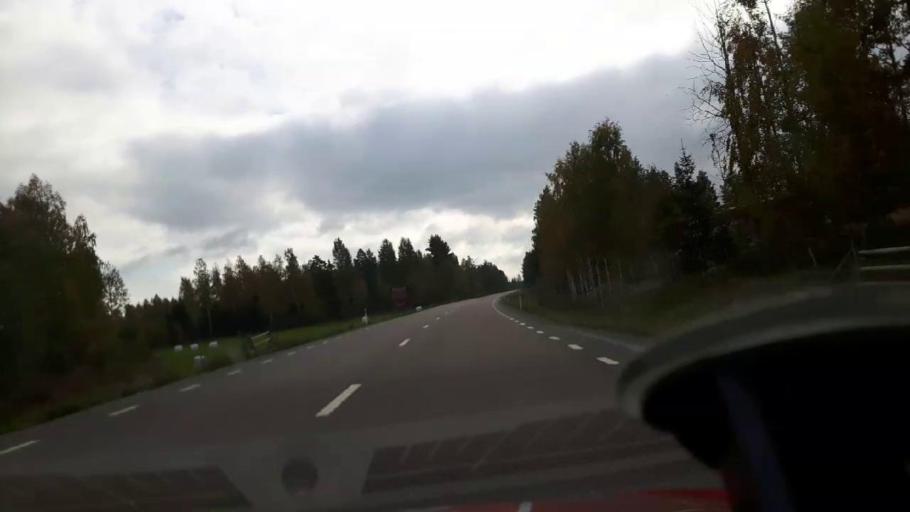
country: SE
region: Gaevleborg
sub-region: Bollnas Kommun
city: Kilafors
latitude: 61.2832
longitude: 16.5183
